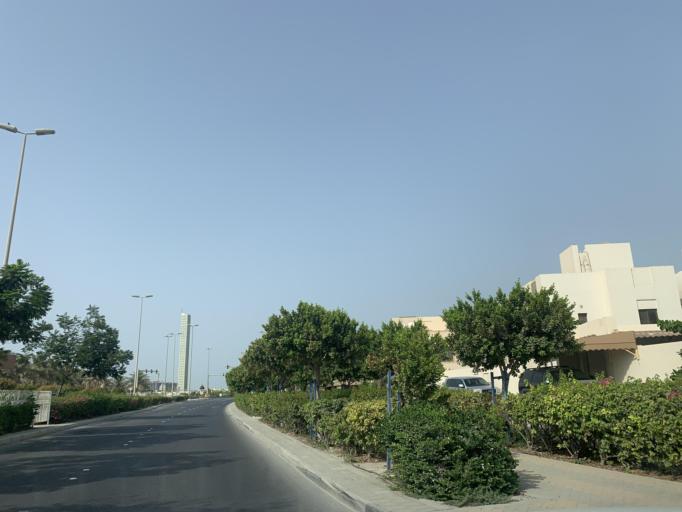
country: BH
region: Manama
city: Jidd Hafs
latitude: 26.2264
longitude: 50.4487
